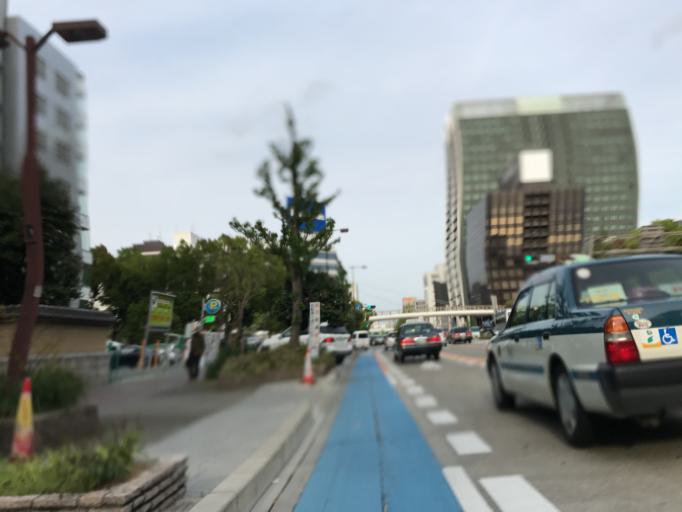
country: JP
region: Aichi
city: Nagoya-shi
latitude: 35.1738
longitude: 136.9071
